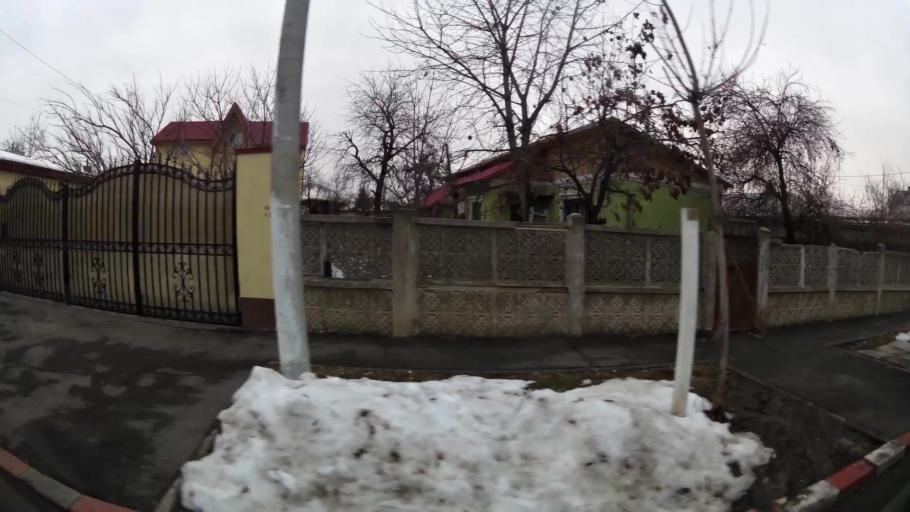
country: RO
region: Ilfov
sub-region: Voluntari City
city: Voluntari
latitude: 44.4890
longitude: 26.1761
